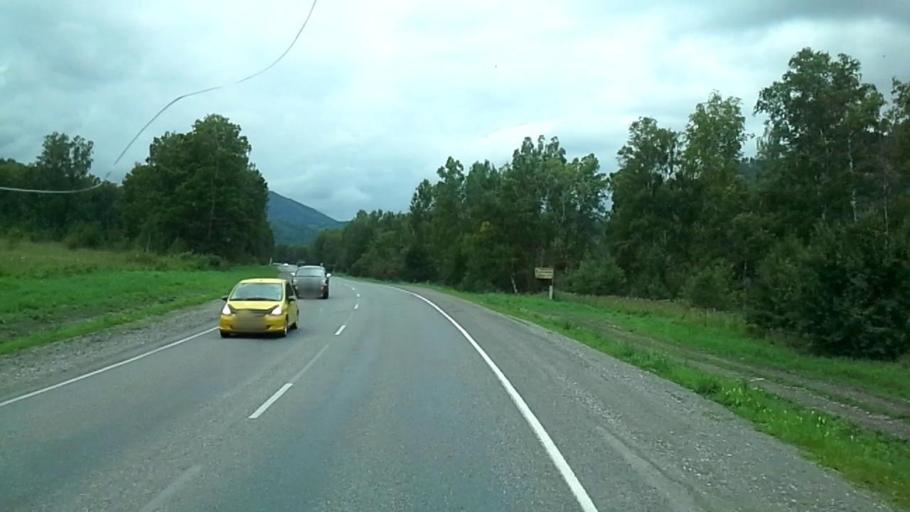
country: RU
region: Altay
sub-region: Mayminskiy Rayon
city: Manzherok
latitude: 51.8548
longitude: 85.7463
